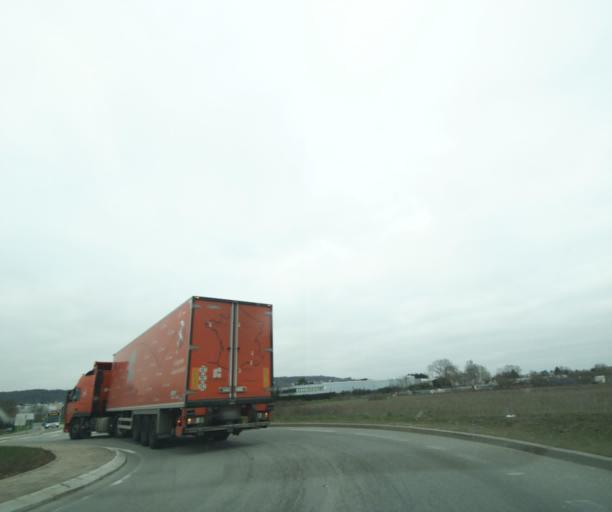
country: FR
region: Ile-de-France
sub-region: Departement des Yvelines
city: Chanteloup-les-Vignes
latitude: 48.9648
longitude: 2.0339
